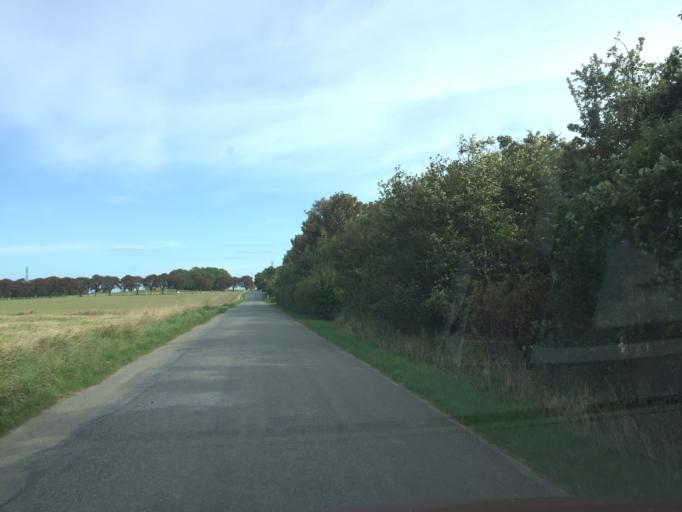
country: DK
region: Zealand
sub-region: Kalundborg Kommune
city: Kalundborg
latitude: 55.6341
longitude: 11.1096
